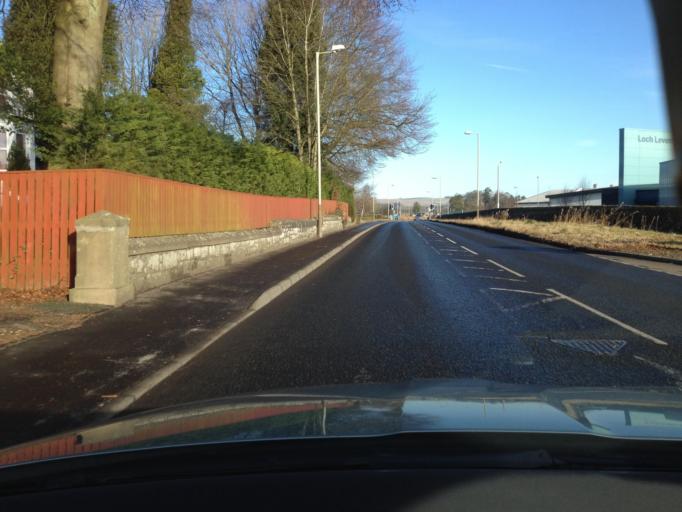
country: GB
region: Scotland
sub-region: Perth and Kinross
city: Kinross
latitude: 56.2156
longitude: -3.4269
